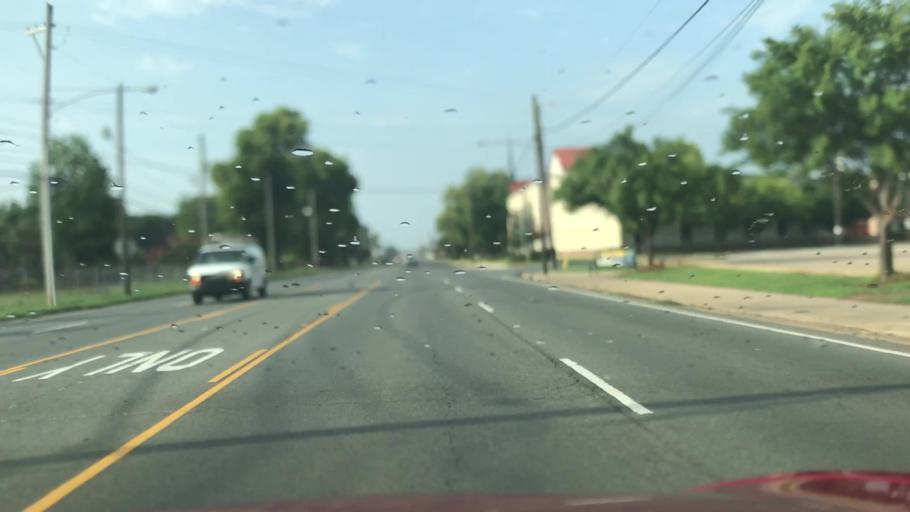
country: US
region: Louisiana
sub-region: Bossier Parish
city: Bossier City
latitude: 32.4656
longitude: -93.7222
